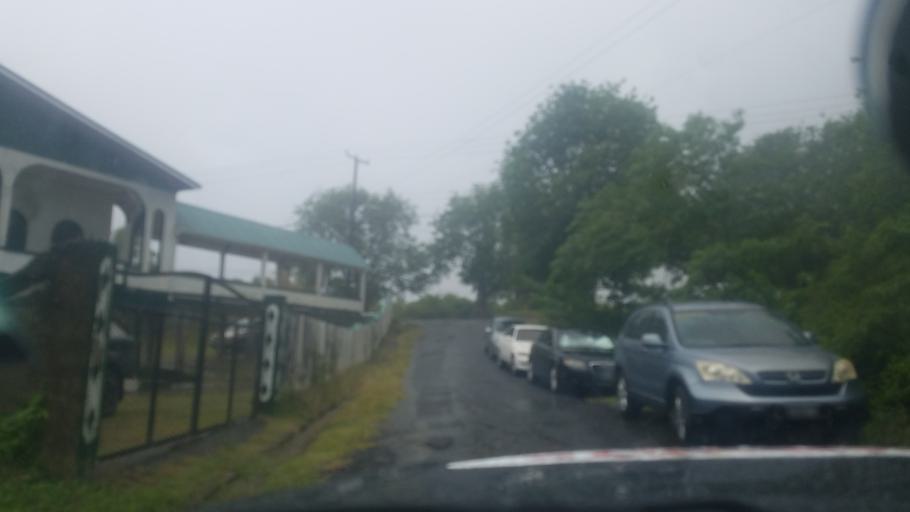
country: LC
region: Laborie Quarter
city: Laborie
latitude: 13.7442
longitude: -60.9704
